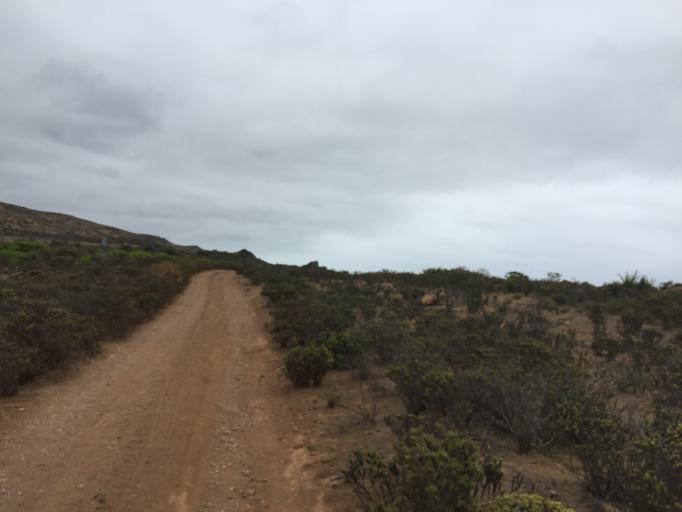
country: CL
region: Valparaiso
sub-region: Petorca Province
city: La Ligua
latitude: -32.1659
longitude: -71.5199
